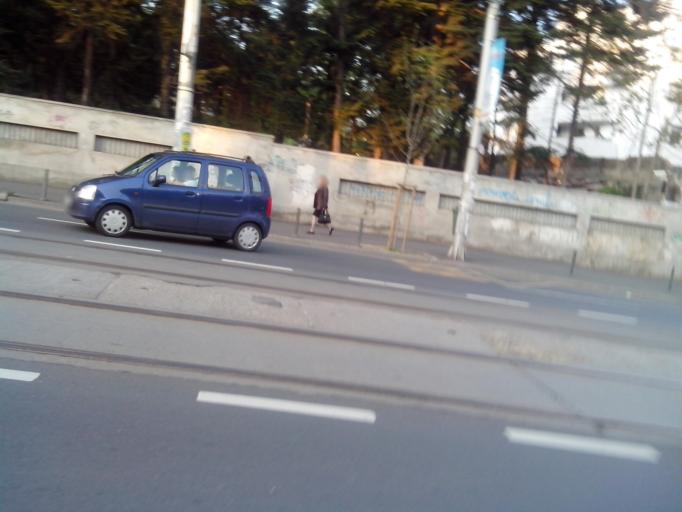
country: RO
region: Bucuresti
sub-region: Municipiul Bucuresti
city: Bucuresti
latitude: 44.4554
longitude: 26.0809
